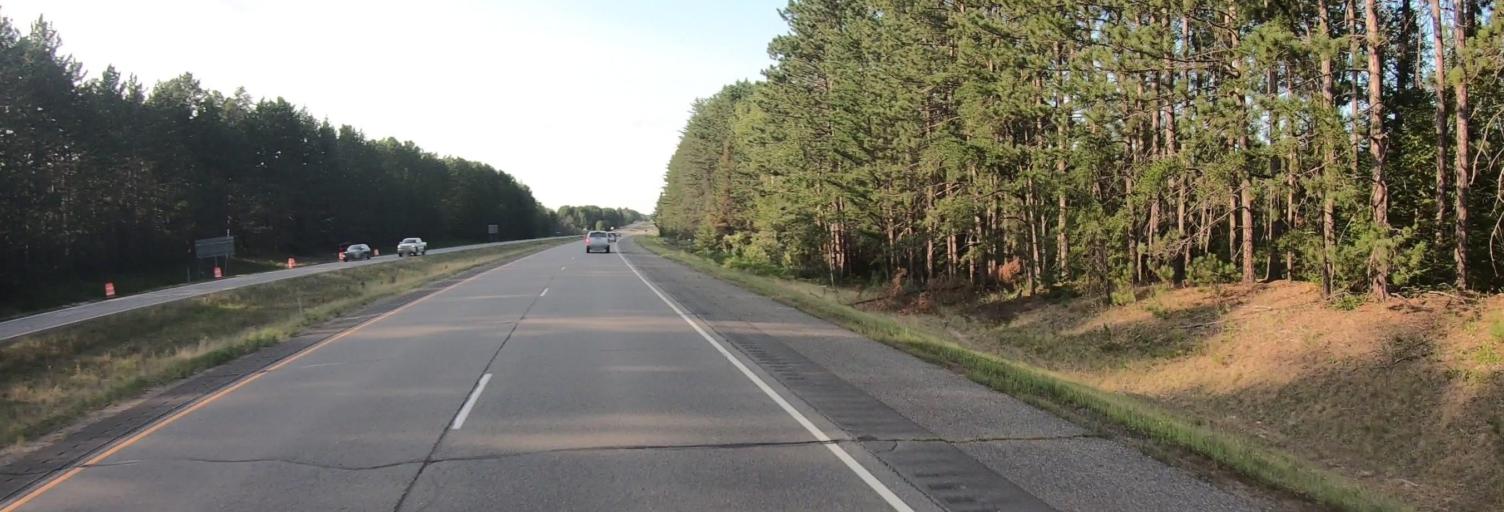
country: US
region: Minnesota
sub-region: Saint Louis County
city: Eveleth
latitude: 47.4060
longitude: -92.5196
